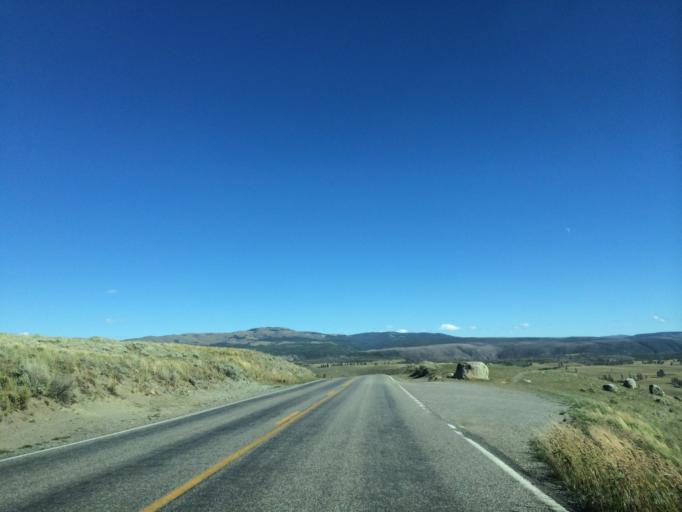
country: US
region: Montana
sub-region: Gallatin County
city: West Yellowstone
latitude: 44.8535
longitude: -110.4175
